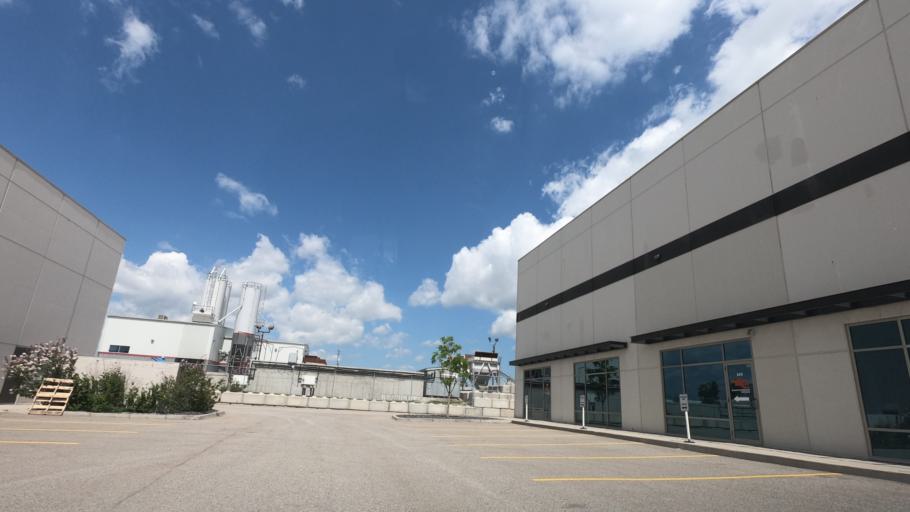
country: CA
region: Alberta
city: Airdrie
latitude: 51.2965
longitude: -113.9878
